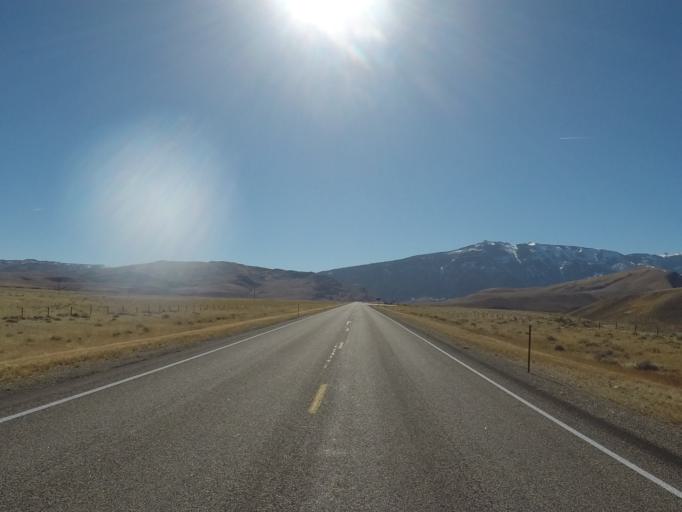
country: US
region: Wyoming
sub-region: Park County
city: Cody
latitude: 44.7311
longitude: -109.2293
